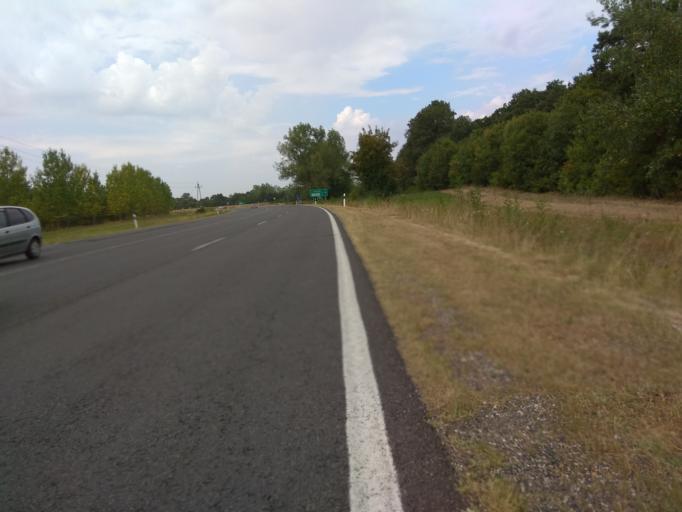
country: HU
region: Borsod-Abauj-Zemplen
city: Harsany
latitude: 47.9214
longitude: 20.7271
